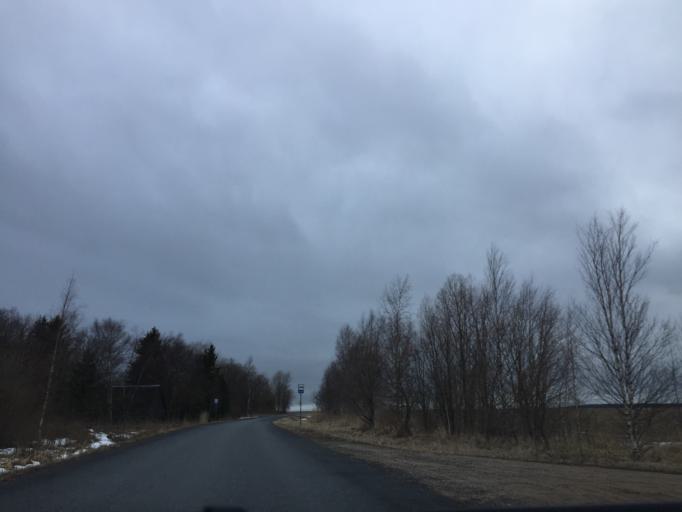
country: EE
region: Laeaene
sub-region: Haapsalu linn
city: Haapsalu
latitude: 58.8009
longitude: 23.5124
